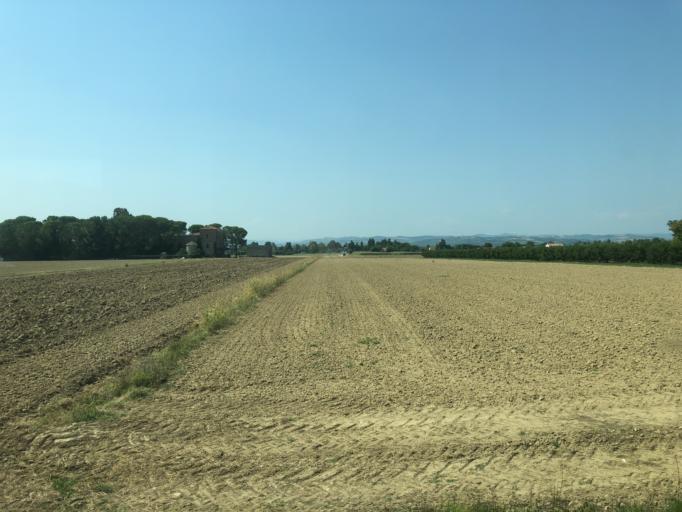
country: IT
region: Emilia-Romagna
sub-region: Forli-Cesena
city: Forlimpopoli
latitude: 44.2046
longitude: 12.1027
